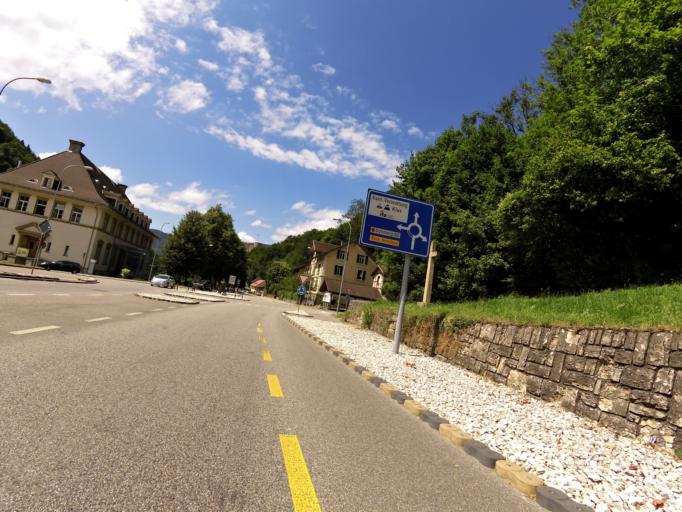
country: CH
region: Solothurn
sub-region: Bezirk Thal
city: Balsthal
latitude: 47.3043
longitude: 7.6951
